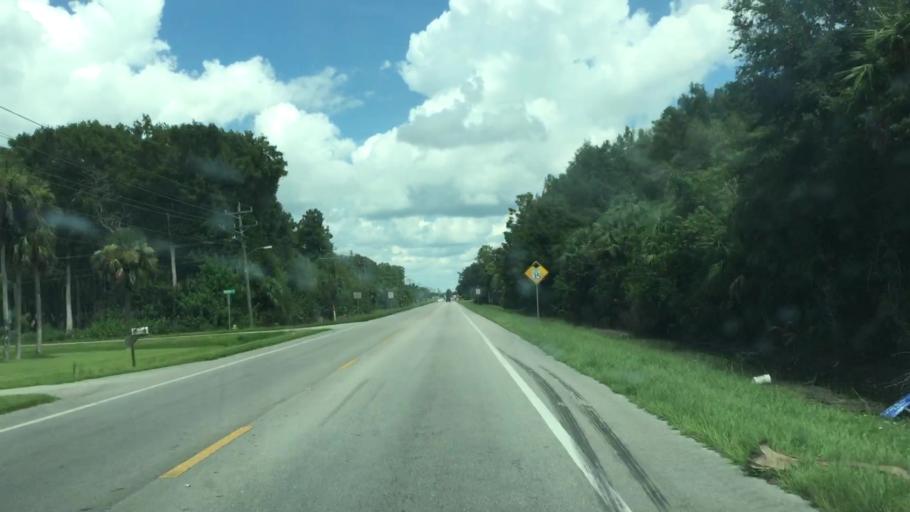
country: US
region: Florida
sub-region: Collier County
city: Immokalee
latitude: 26.4036
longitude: -81.4171
